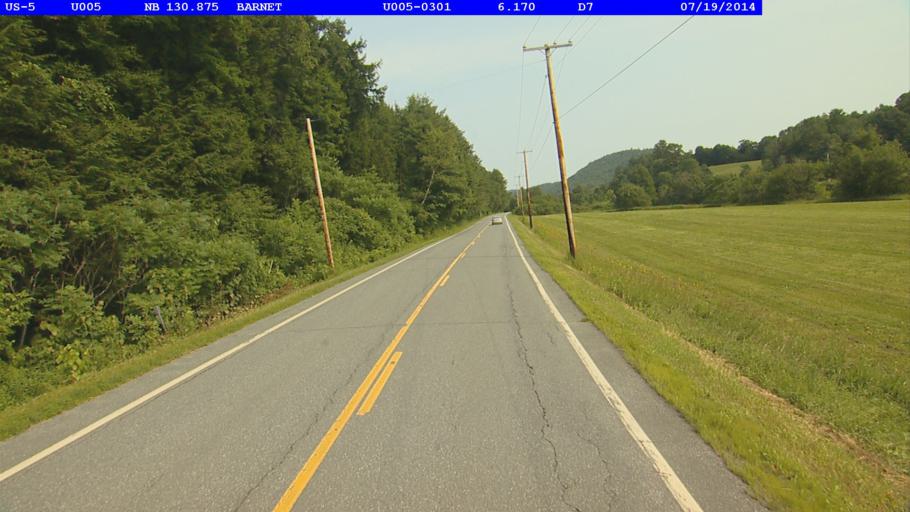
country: US
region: Vermont
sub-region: Caledonia County
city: Saint Johnsbury
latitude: 44.3331
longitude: -72.0420
